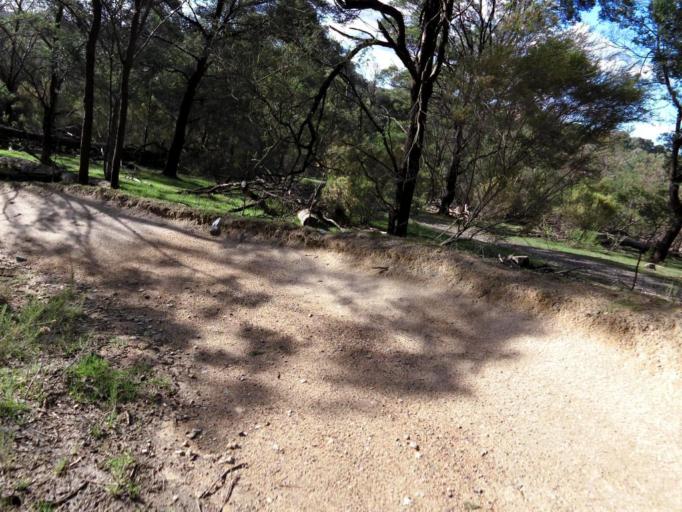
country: AU
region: Victoria
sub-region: Yarra Ranges
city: Lysterfield
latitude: -37.9459
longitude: 145.2741
